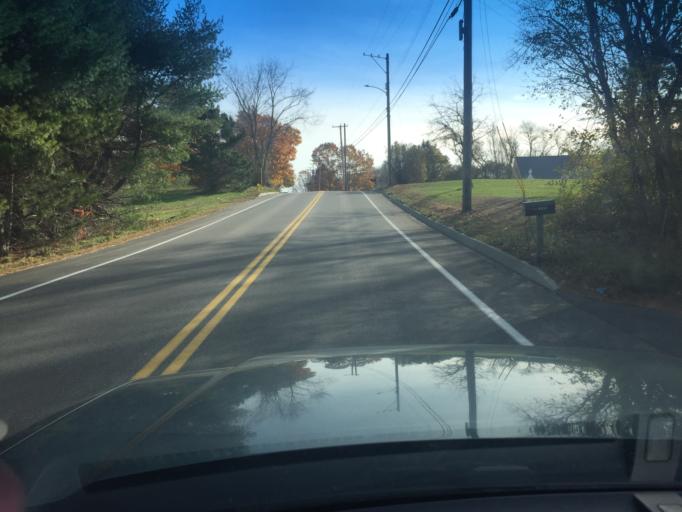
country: US
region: Maine
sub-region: York County
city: York Harbor
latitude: 43.1605
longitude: -70.7037
